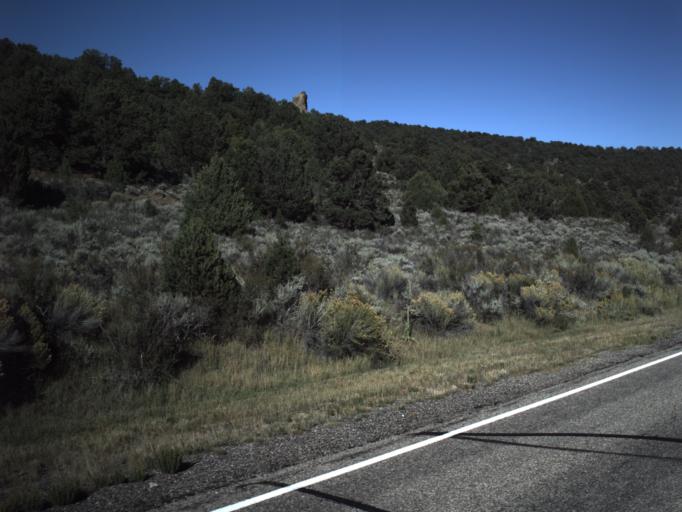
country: US
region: Utah
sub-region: Garfield County
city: Panguitch
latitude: 37.7623
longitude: -112.5250
